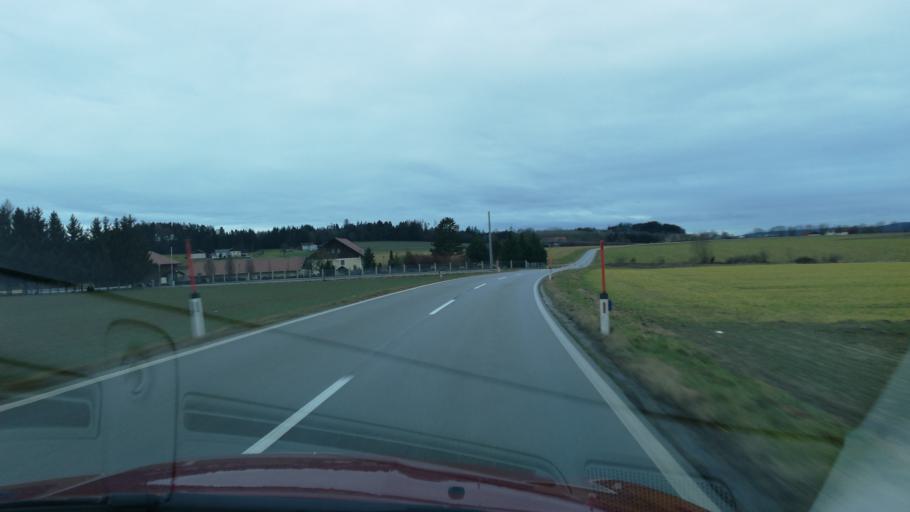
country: DE
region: Bavaria
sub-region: Lower Bavaria
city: Bad Fussing
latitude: 48.2658
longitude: 13.3242
